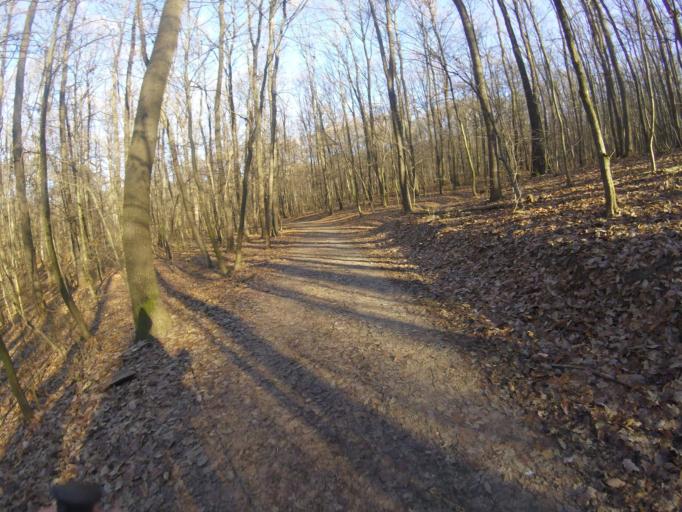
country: HU
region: Pest
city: Budakeszi
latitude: 47.5466
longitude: 18.9698
